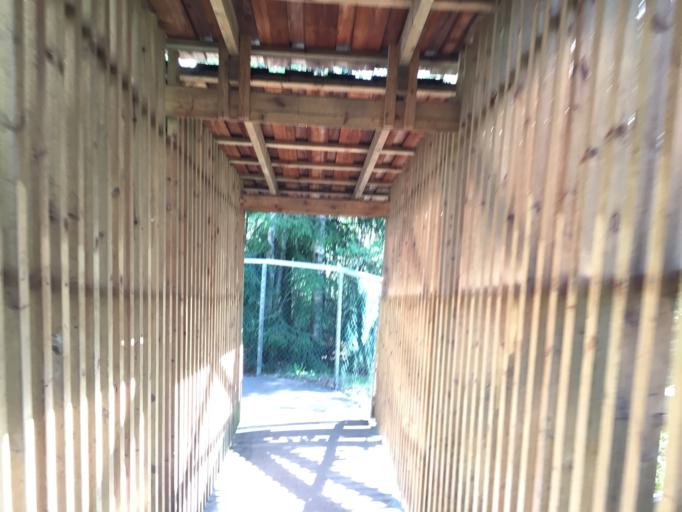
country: NO
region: Akershus
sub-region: Ski
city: Ski
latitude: 59.7472
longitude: 10.7768
